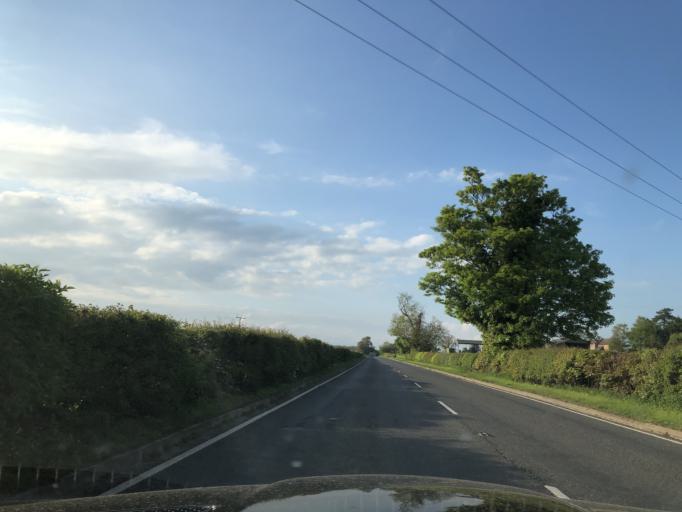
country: GB
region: England
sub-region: Warwickshire
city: Shipston on Stour
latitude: 52.1170
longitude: -1.6198
